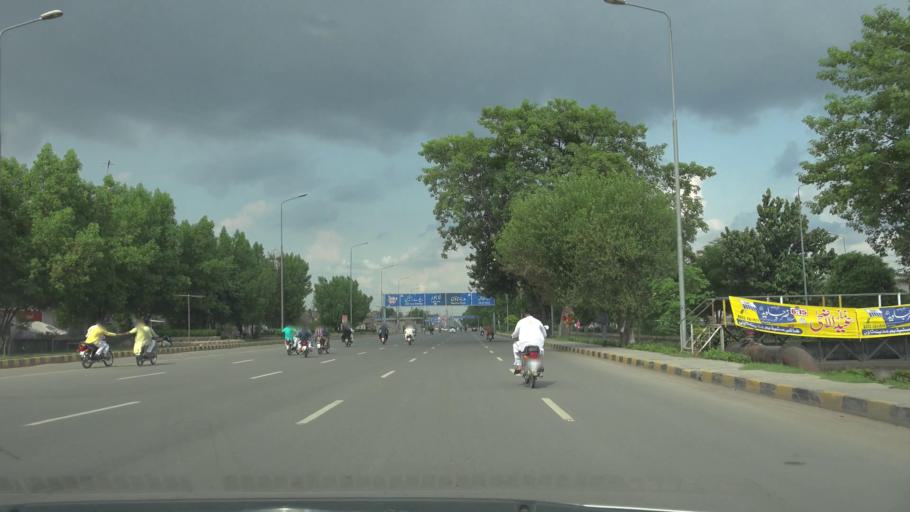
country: PK
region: Punjab
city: Faisalabad
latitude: 31.4224
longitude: 73.1093
